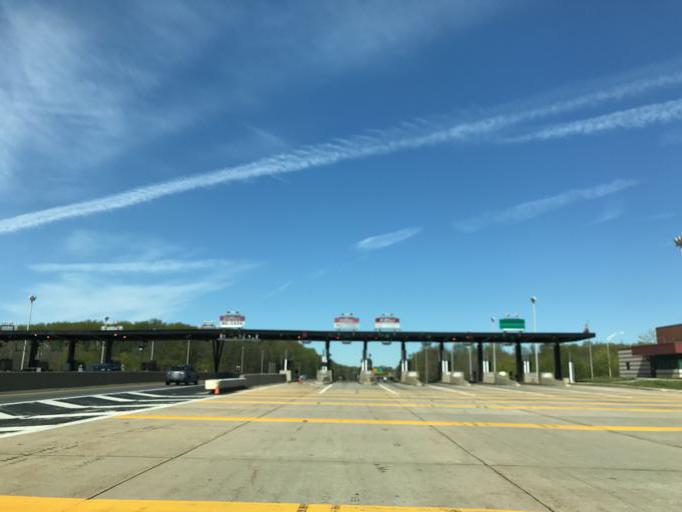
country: US
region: New Jersey
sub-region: Burlington County
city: Roebling
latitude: 40.0965
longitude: -74.7768
